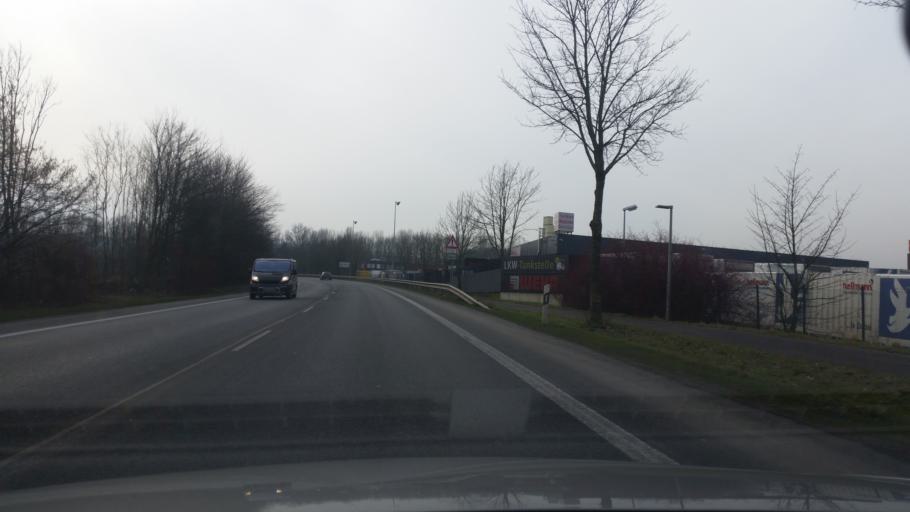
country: DE
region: North Rhine-Westphalia
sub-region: Regierungsbezirk Detmold
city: Oerlinghausen
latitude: 52.0033
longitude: 8.6103
